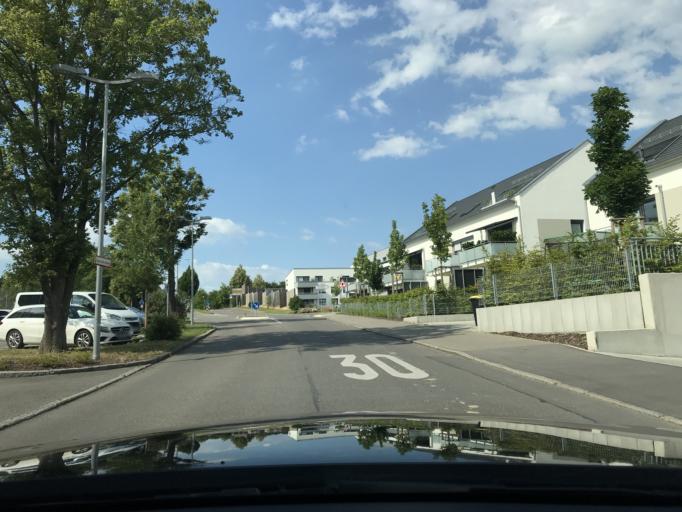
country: DE
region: Baden-Wuerttemberg
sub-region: Regierungsbezirk Stuttgart
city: Waiblingen
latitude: 48.8197
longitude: 9.3070
